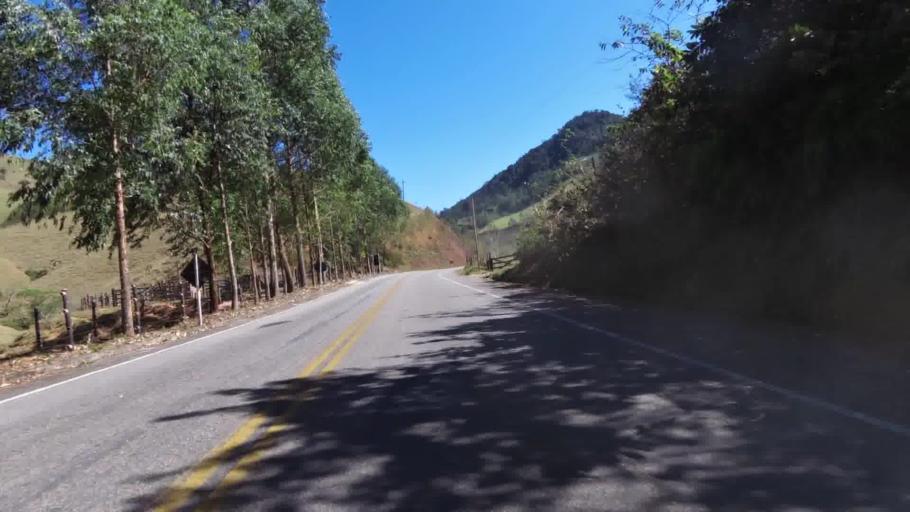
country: BR
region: Espirito Santo
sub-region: Vargem Alta
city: Vargem Alta
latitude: -20.7007
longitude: -40.9303
